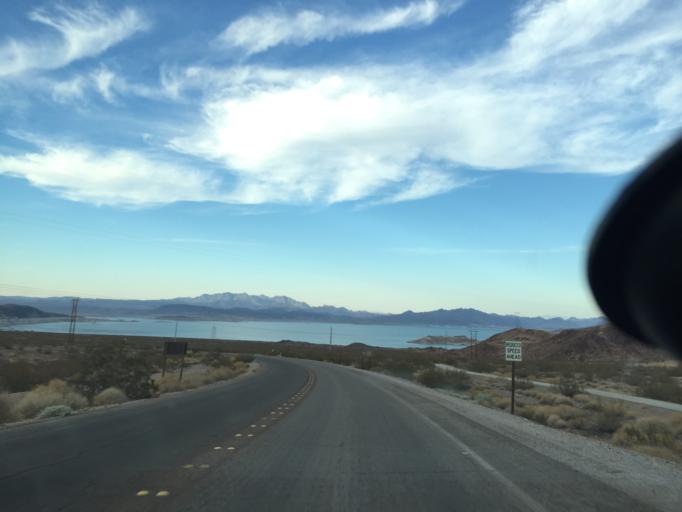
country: US
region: Nevada
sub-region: Clark County
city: Boulder City
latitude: 36.0126
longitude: -114.7941
